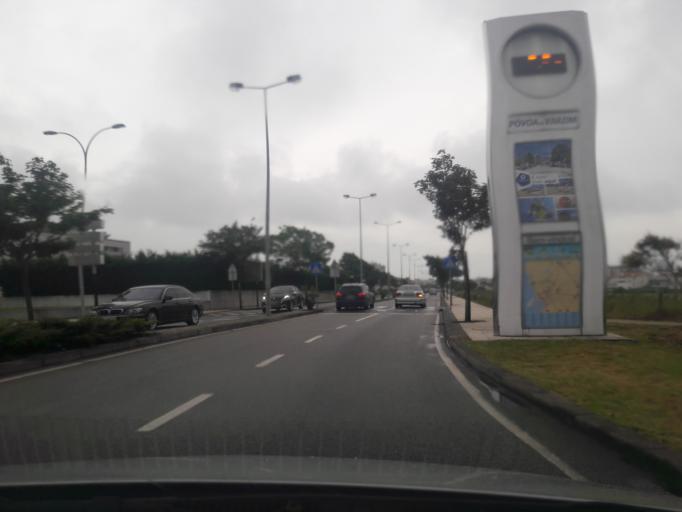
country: PT
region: Porto
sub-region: Povoa de Varzim
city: Povoa de Varzim
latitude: 41.3936
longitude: -8.7578
